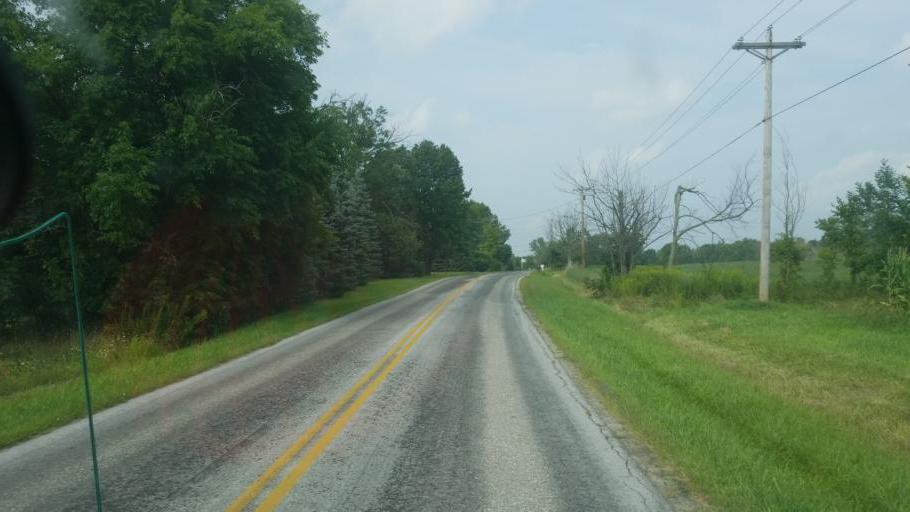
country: US
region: Ohio
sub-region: Wayne County
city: West Salem
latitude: 41.0633
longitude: -82.1626
